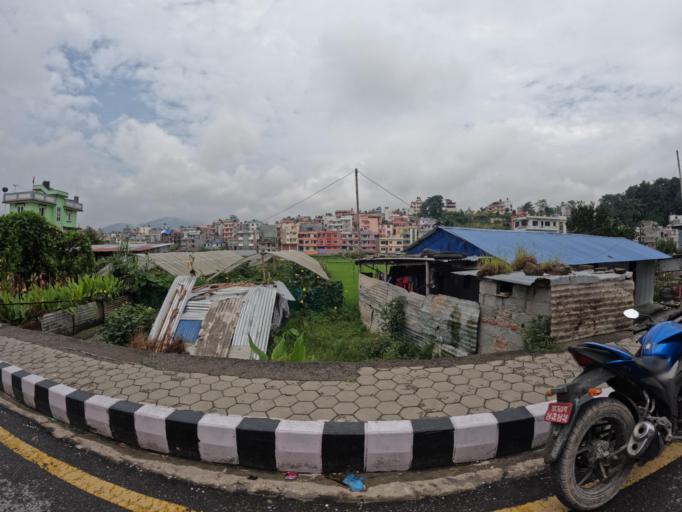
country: NP
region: Central Region
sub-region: Bagmati Zone
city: Kathmandu
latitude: 27.7577
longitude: 85.3251
